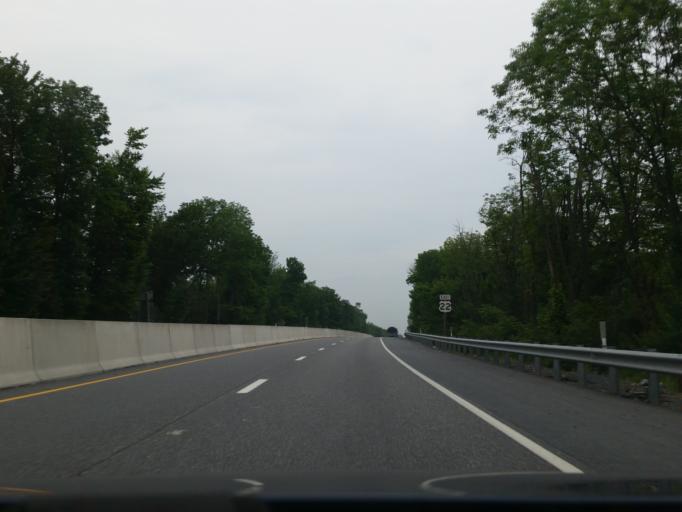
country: US
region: Pennsylvania
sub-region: Lebanon County
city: Jonestown
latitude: 40.4189
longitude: -76.4948
